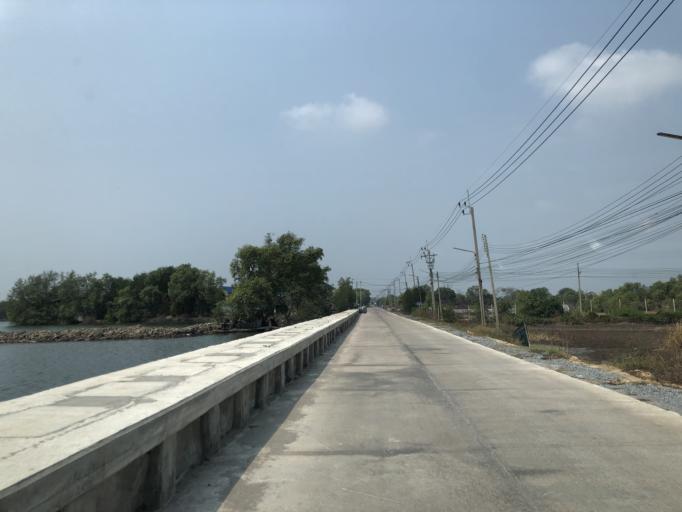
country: TH
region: Samut Prakan
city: Bang Bo
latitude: 13.5174
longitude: 100.8320
